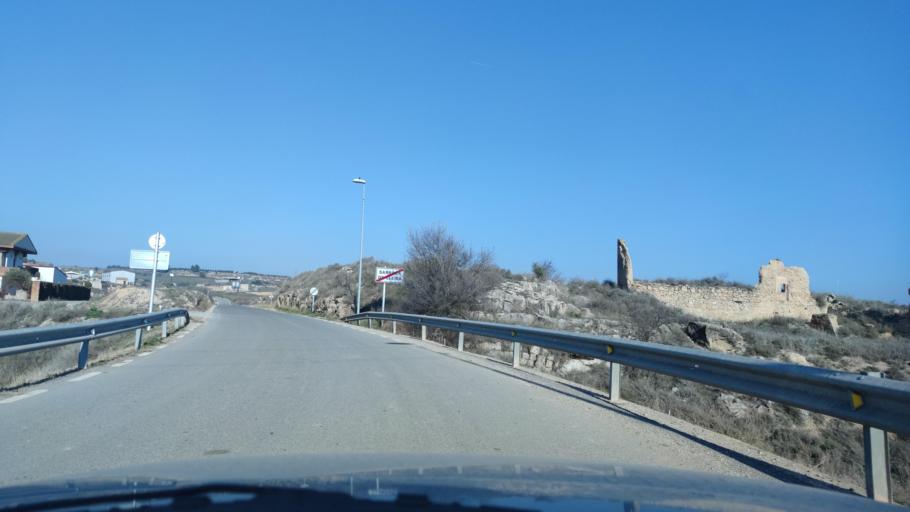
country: ES
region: Catalonia
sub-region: Provincia de Lleida
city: Torrebesses
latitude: 41.4607
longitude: 0.5636
